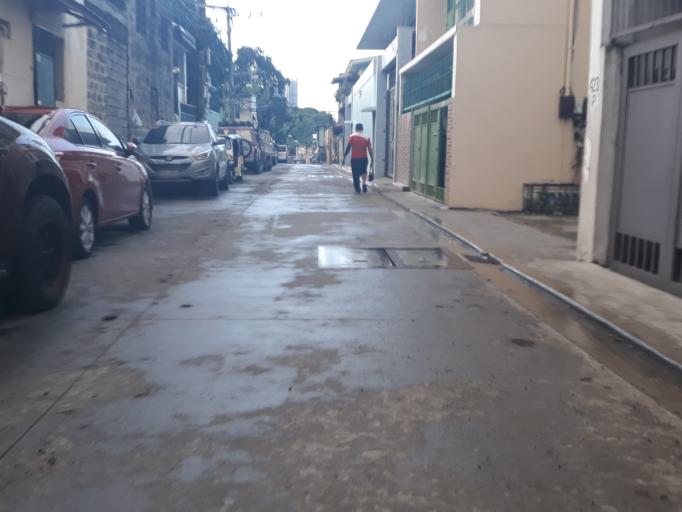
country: PH
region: Metro Manila
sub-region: San Juan
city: San Juan
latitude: 14.6110
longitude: 121.0264
